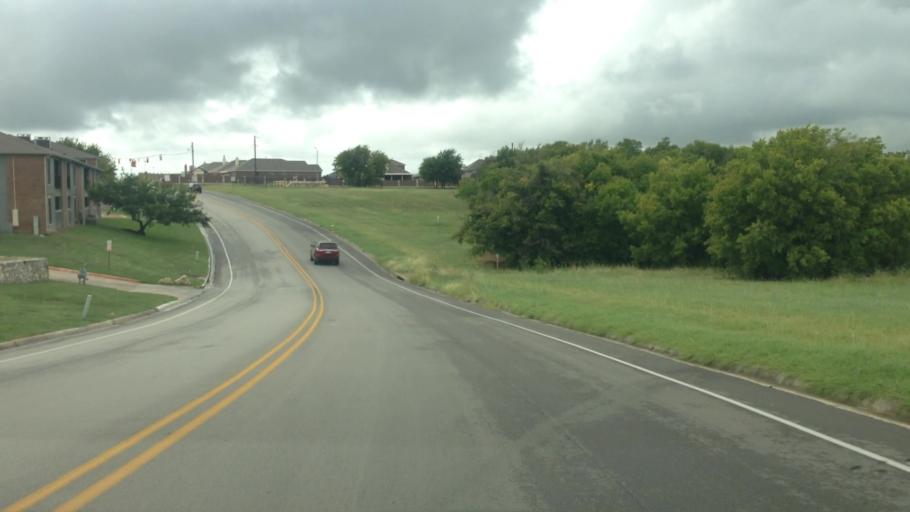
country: US
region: Texas
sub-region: Tarrant County
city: White Settlement
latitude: 32.7432
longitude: -97.4666
